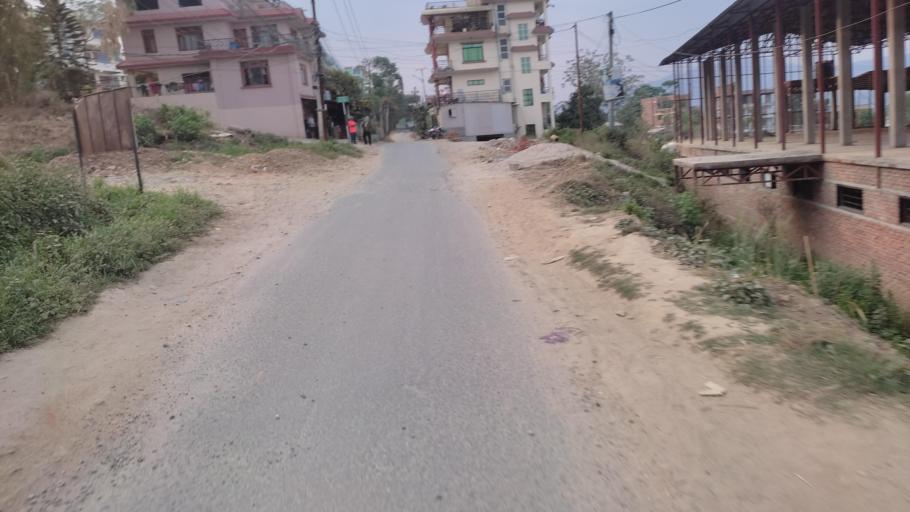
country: NP
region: Central Region
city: Kirtipur
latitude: 27.6715
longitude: 85.2477
